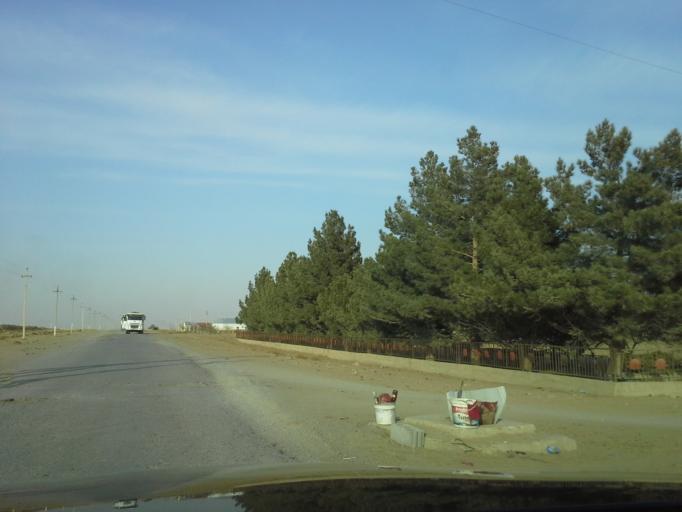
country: TM
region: Ahal
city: Abadan
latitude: 38.1787
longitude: 58.0394
